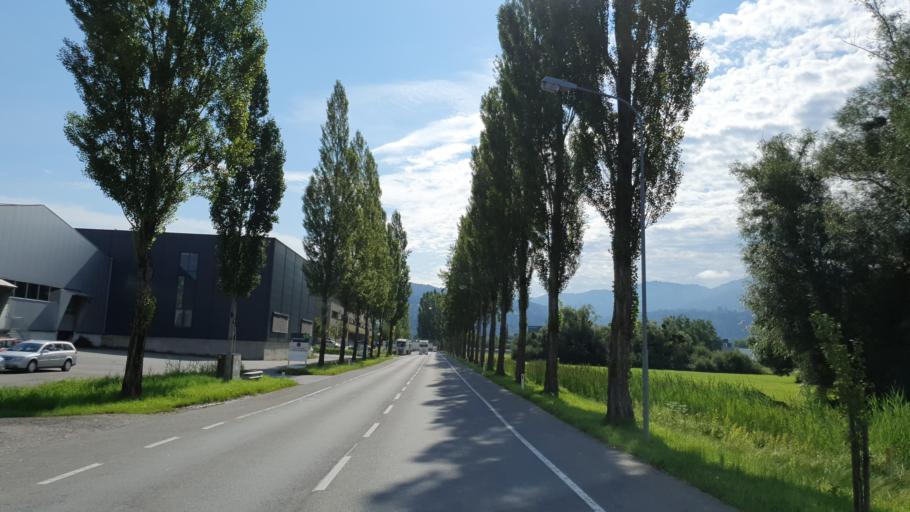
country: AT
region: Vorarlberg
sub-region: Politischer Bezirk Bregenz
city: Wolfurt
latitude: 47.4554
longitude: 9.7353
